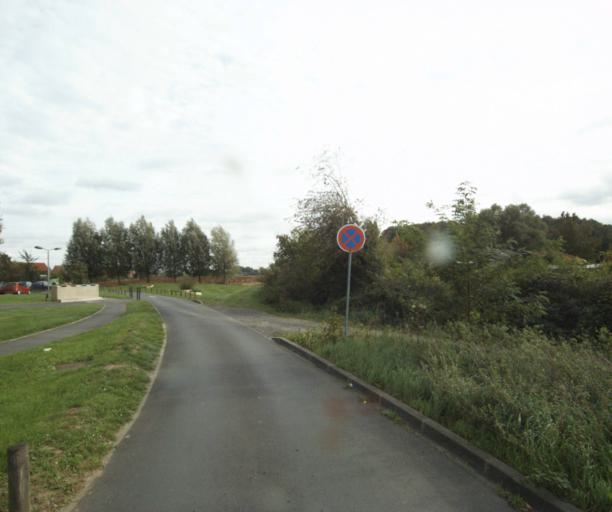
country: FR
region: Nord-Pas-de-Calais
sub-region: Departement du Nord
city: Armentieres
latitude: 50.6709
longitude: 2.8878
